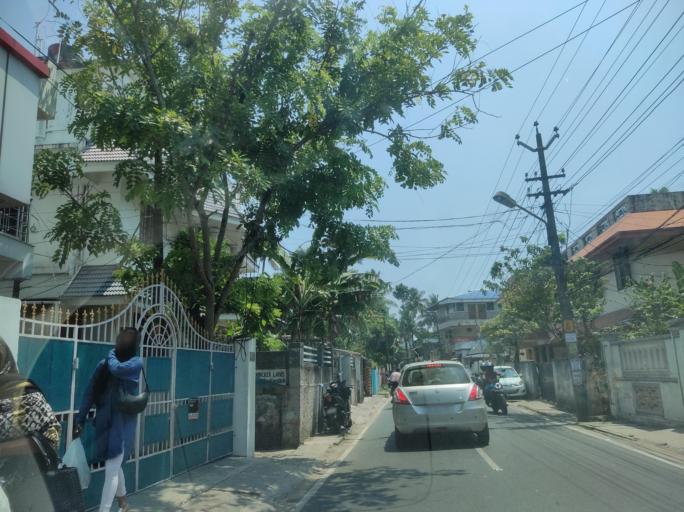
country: IN
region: Kerala
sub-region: Ernakulam
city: Cochin
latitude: 9.9076
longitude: 76.2804
